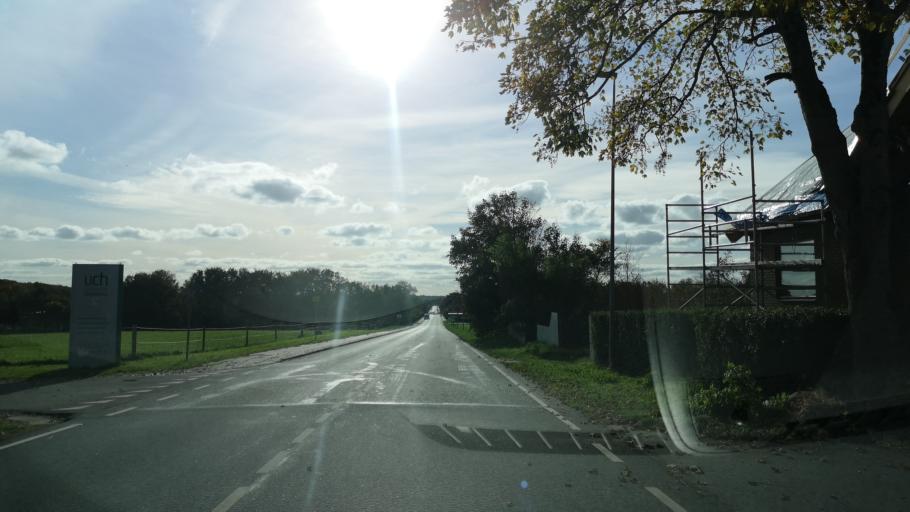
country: DK
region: Central Jutland
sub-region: Holstebro Kommune
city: Holstebro
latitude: 56.3745
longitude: 8.6368
